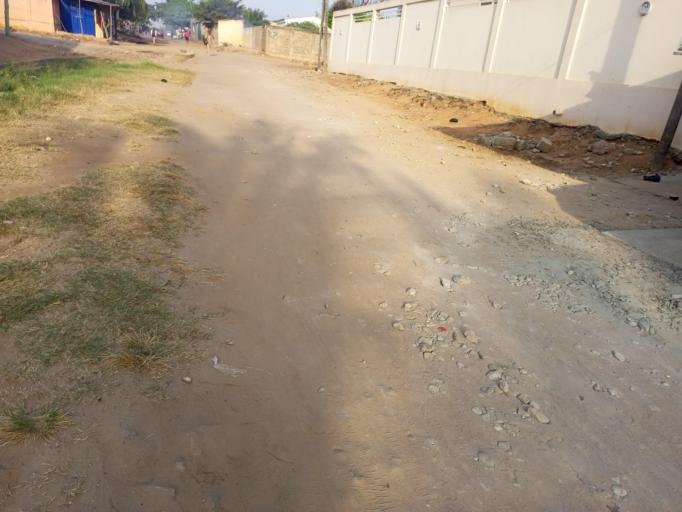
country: TG
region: Maritime
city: Lome
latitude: 6.1730
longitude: 1.2061
